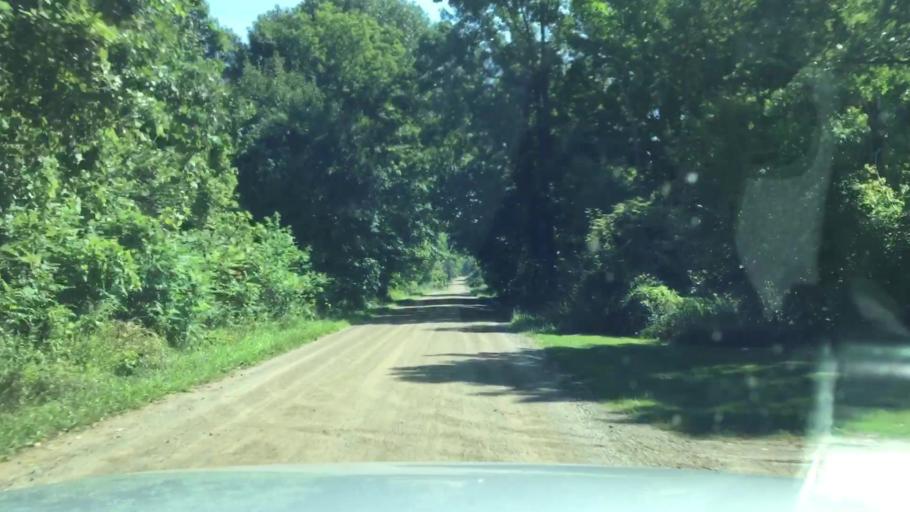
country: US
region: Michigan
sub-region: Lenawee County
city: Manitou Beach-Devils Lake
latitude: 41.9936
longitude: -84.3319
